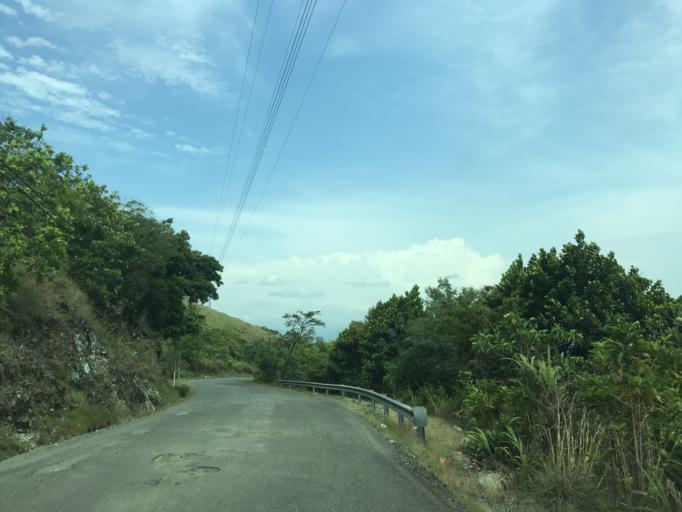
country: GT
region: Izabal
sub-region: Municipio de Los Amates
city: Los Amates
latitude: 15.3868
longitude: -89.0256
